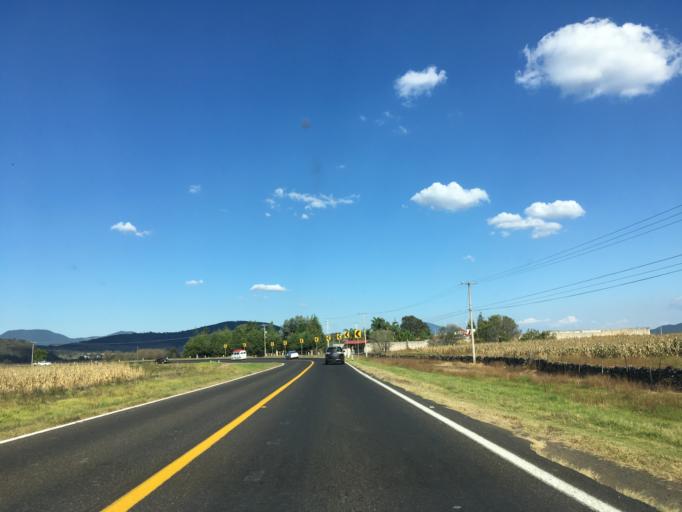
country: MX
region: Michoacan
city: Patzcuaro
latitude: 19.5666
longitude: -101.5732
